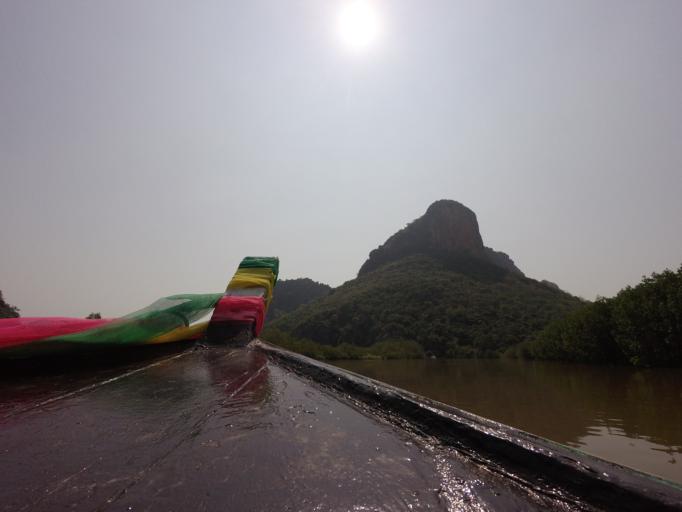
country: TH
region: Prachuap Khiri Khan
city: Kui Buri
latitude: 12.1438
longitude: 99.9519
